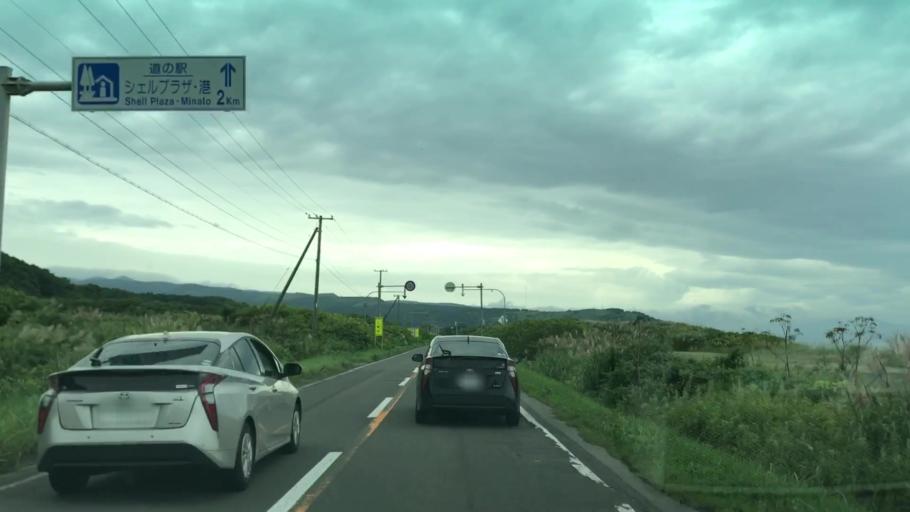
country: JP
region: Hokkaido
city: Iwanai
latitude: 42.8951
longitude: 140.3773
